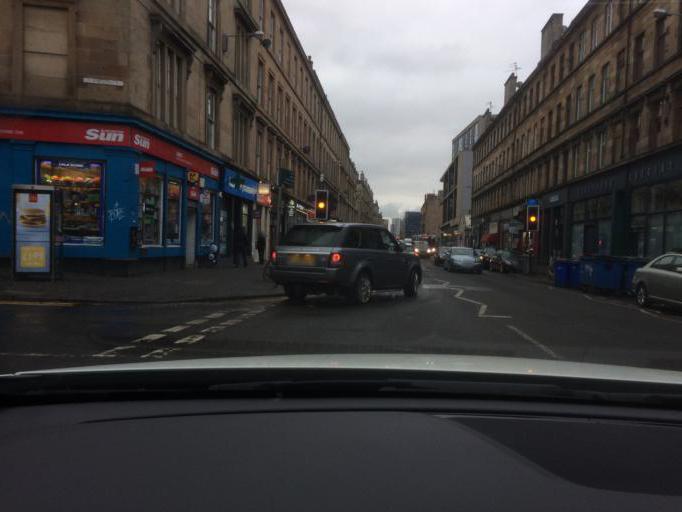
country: GB
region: Scotland
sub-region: Glasgow City
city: Glasgow
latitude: 55.8648
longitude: -4.2841
